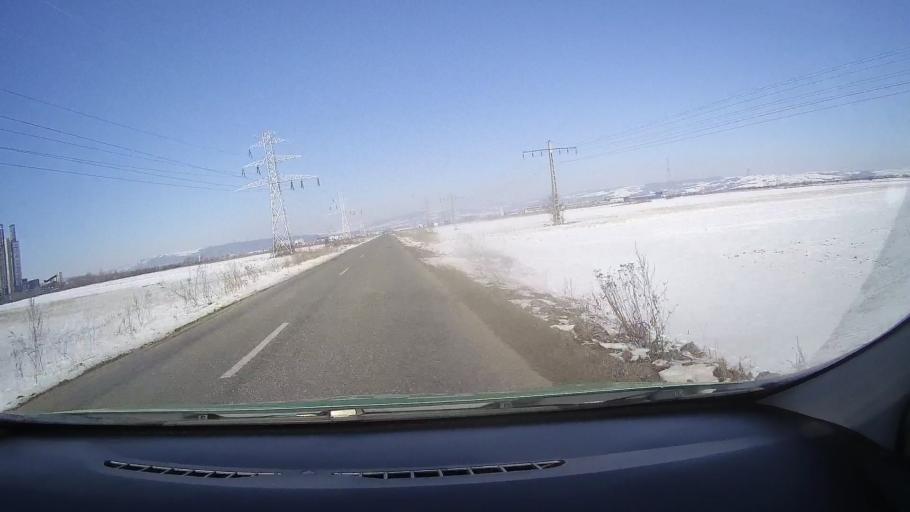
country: RO
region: Brasov
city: Fogarasch
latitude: 45.8117
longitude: 24.9891
